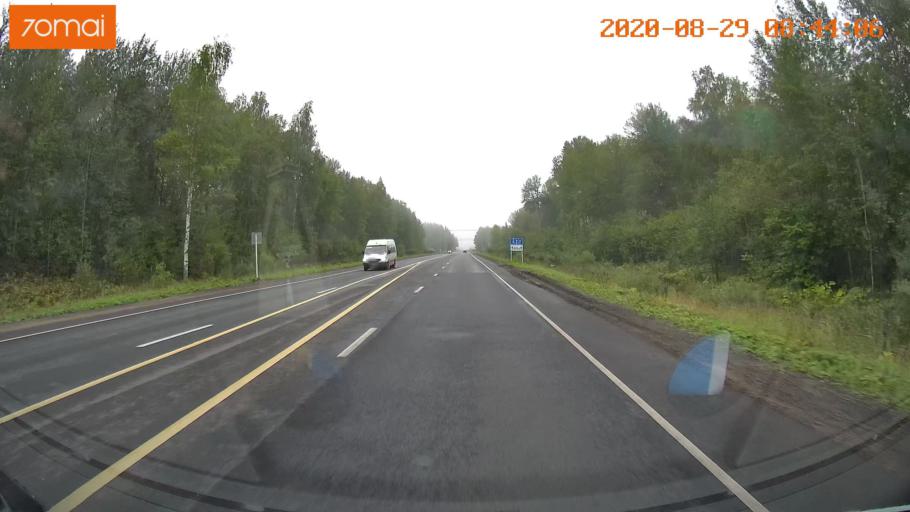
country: RU
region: Ivanovo
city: Rodniki
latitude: 57.1138
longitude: 41.7850
